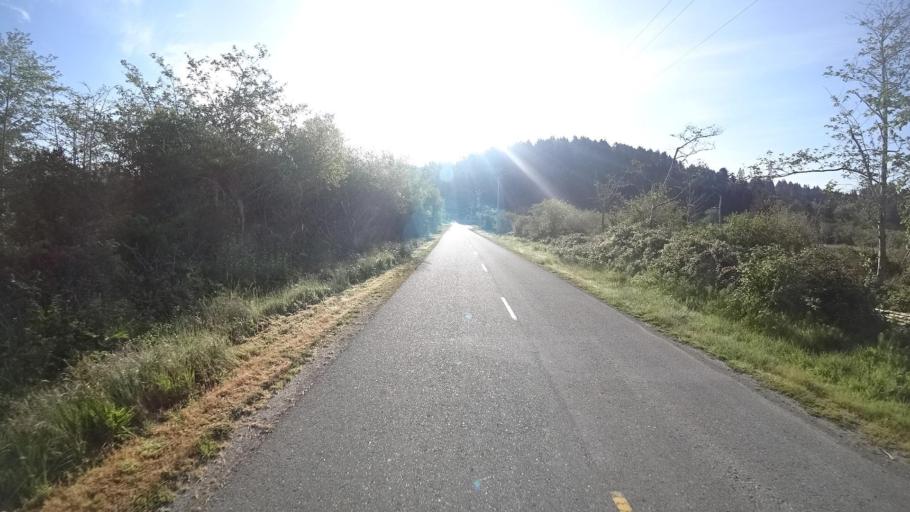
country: US
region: California
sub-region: Humboldt County
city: Humboldt Hill
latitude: 40.7225
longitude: -124.2179
